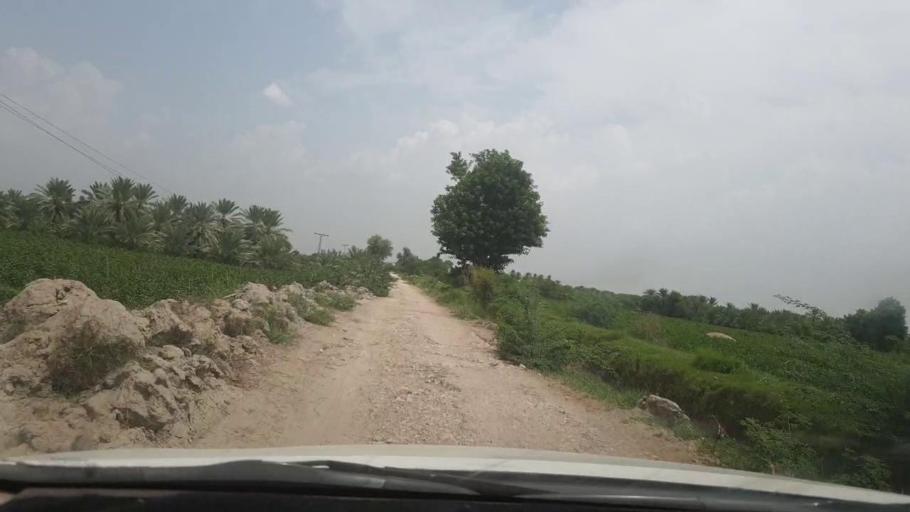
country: PK
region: Sindh
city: Khairpur
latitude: 27.3722
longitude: 68.9967
